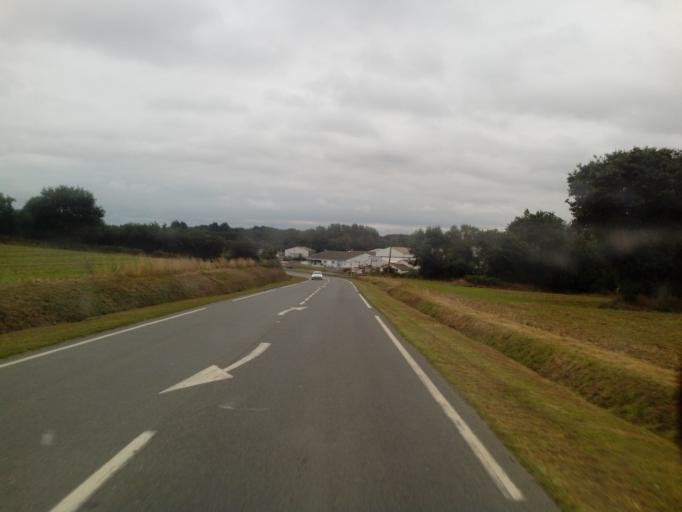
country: FR
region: Brittany
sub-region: Departement des Cotes-d'Armor
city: Plouha
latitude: 48.6697
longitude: -2.9290
